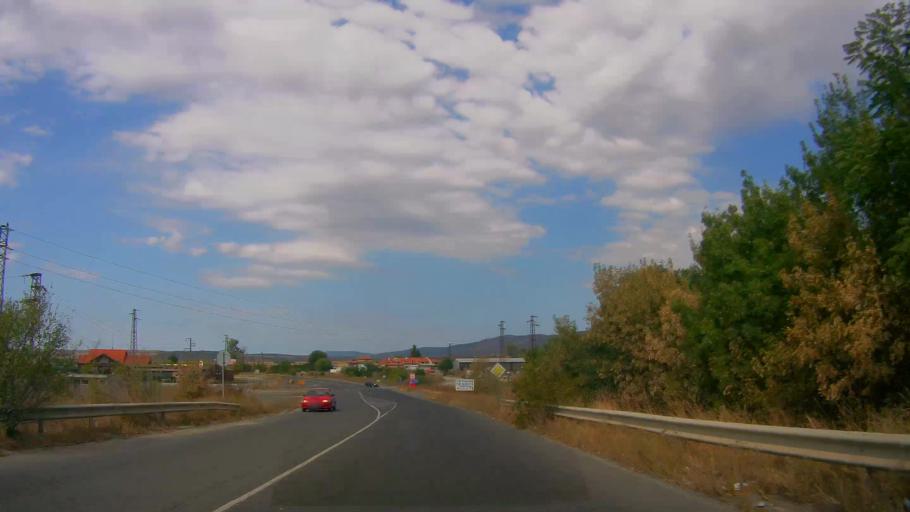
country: BG
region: Burgas
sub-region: Obshtina Aytos
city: Aytos
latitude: 42.7050
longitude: 27.2381
